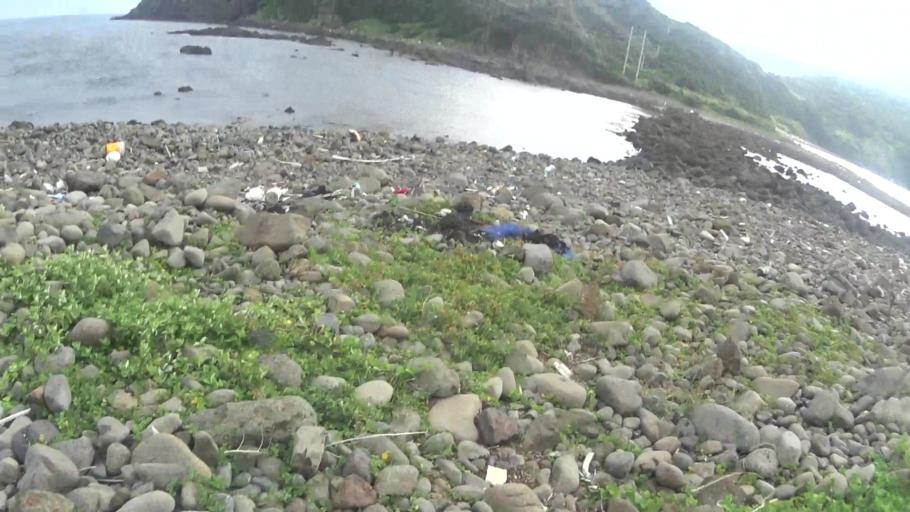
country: JP
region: Nagasaki
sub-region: Hirado Shi
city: Hirado
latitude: 33.1822
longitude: 129.3492
